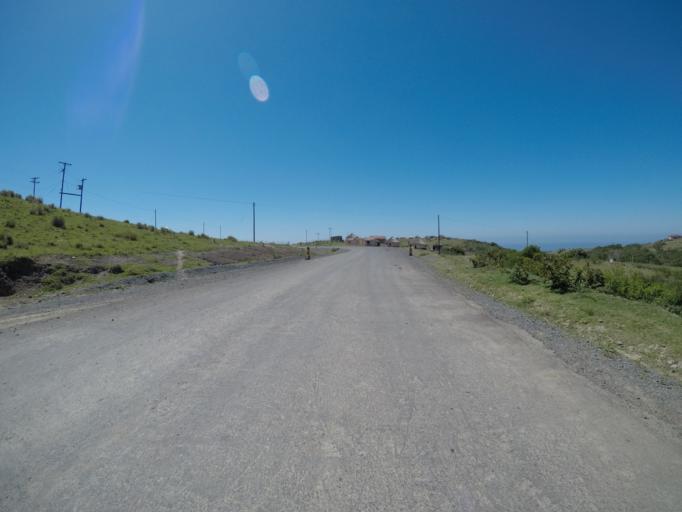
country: ZA
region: Eastern Cape
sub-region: OR Tambo District Municipality
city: Libode
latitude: -31.9988
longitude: 29.1211
